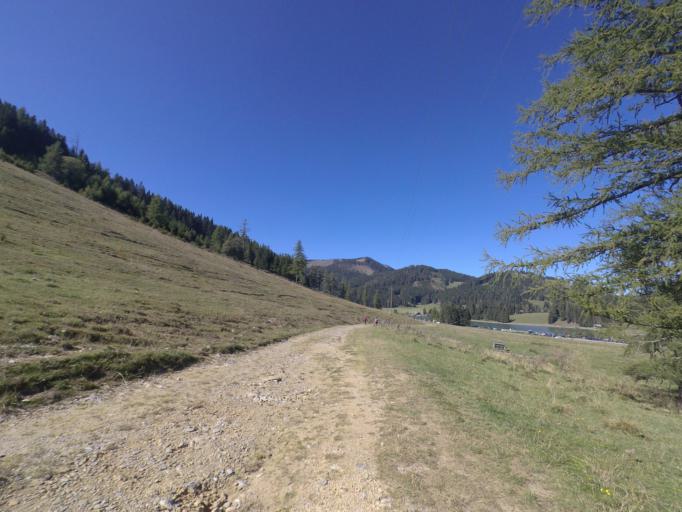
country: AT
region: Styria
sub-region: Politischer Bezirk Weiz
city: Passail
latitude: 47.3450
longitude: 15.4644
